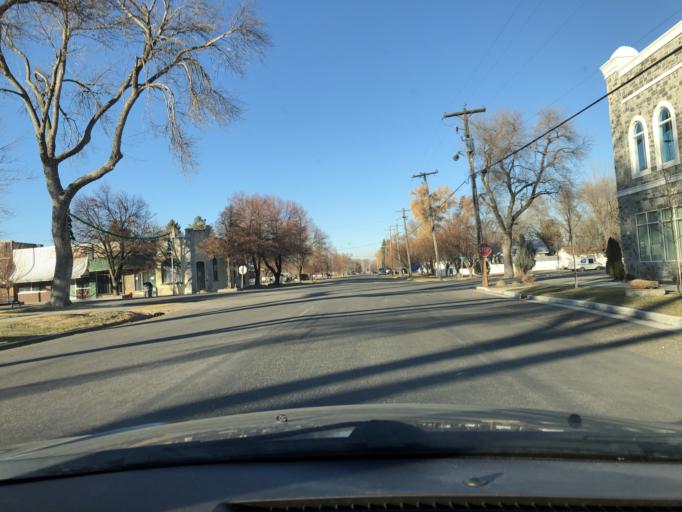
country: US
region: Utah
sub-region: Cache County
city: Wellsville
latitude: 41.6383
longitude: -111.9316
